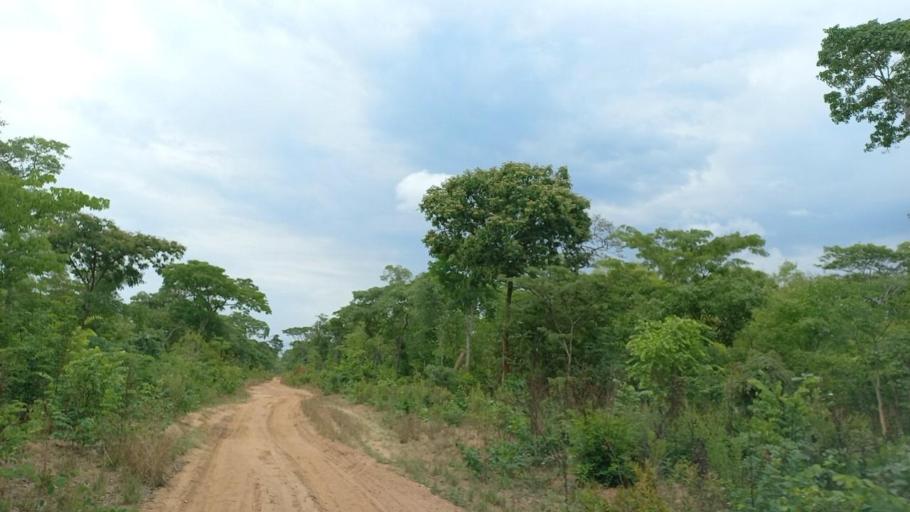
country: ZM
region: North-Western
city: Kalengwa
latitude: -13.5377
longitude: 24.9788
